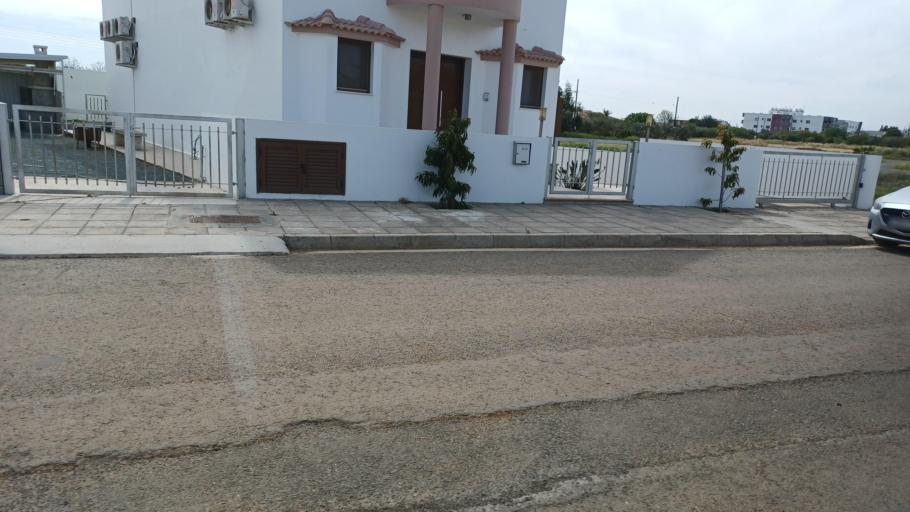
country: CY
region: Lefkosia
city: Kokkinotrimithia
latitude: 35.1522
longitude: 33.2114
